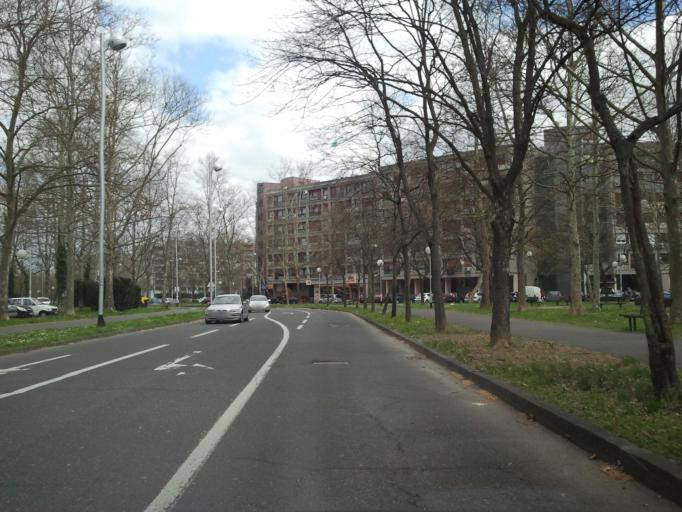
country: HR
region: Grad Zagreb
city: Novi Zagreb
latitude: 45.7661
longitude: 15.9949
